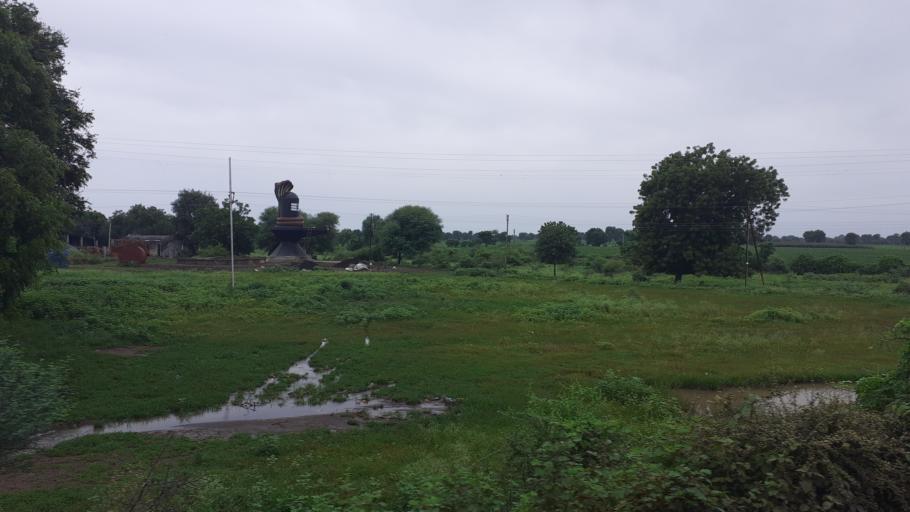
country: IN
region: Maharashtra
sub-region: Buldana
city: Nandura
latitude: 20.8094
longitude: 76.4830
